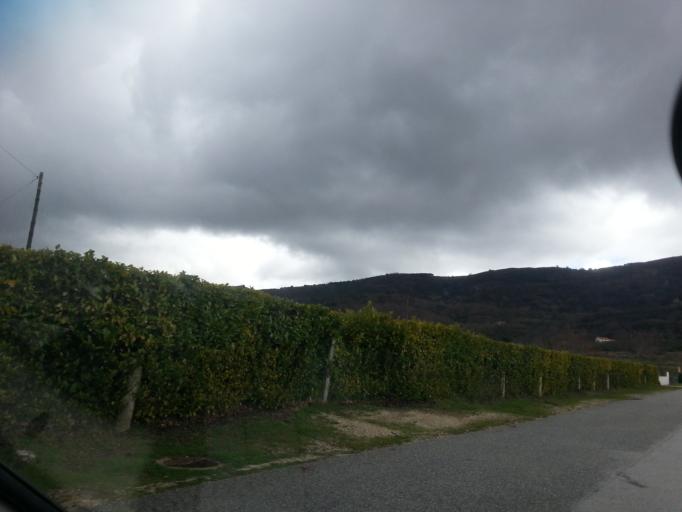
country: PT
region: Guarda
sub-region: Celorico da Beira
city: Celorico da Beira
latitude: 40.5508
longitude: -7.4582
